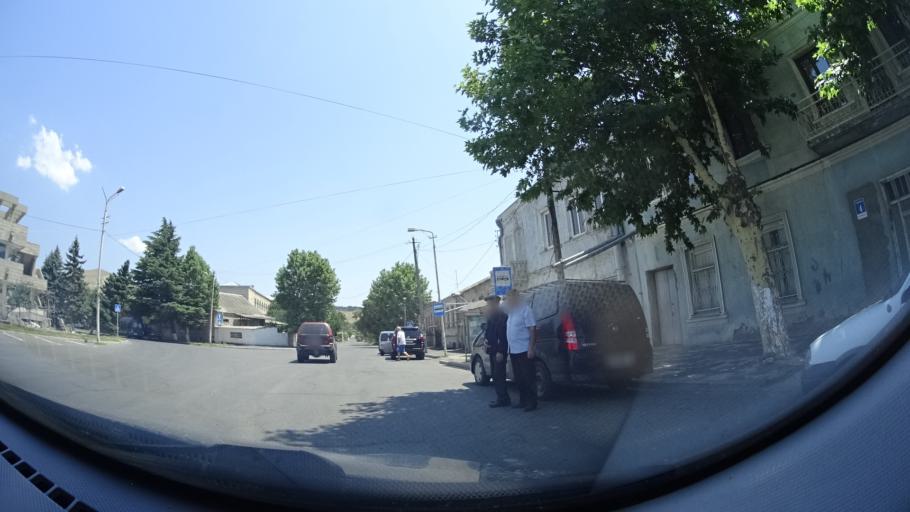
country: GE
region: Shida Kartli
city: Gori
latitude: 41.9884
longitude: 44.1162
